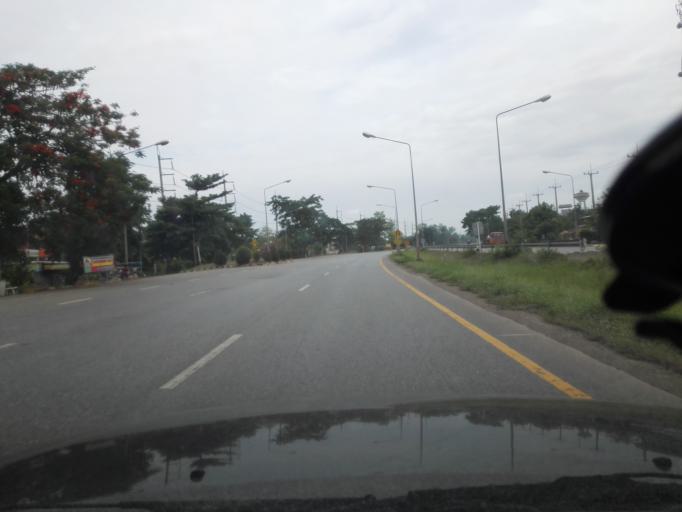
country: TH
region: Kamphaeng Phet
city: Khlong Khlung
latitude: 16.1039
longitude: 99.7191
